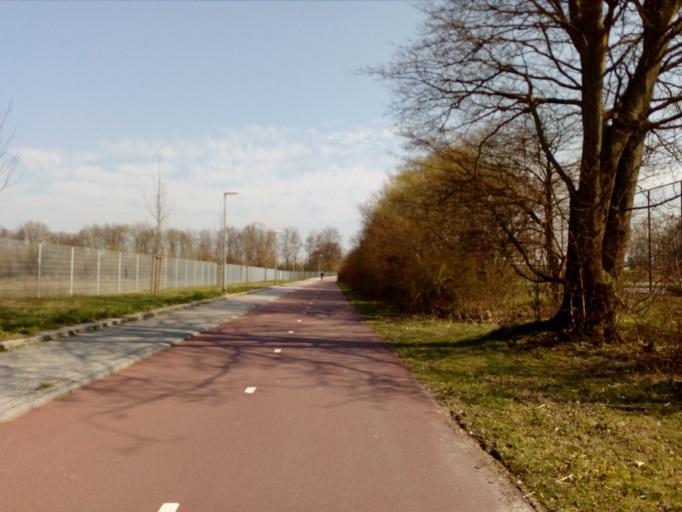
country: NL
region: South Holland
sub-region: Gemeente Zoetermeer
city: Zoetermeer
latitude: 52.0490
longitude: 4.5248
